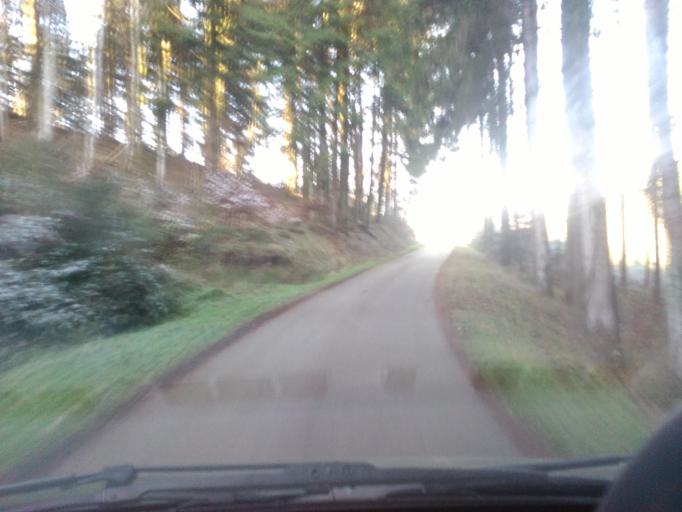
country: FR
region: Lorraine
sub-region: Departement des Vosges
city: Saint-Die-des-Vosges
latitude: 48.3235
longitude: 6.9733
